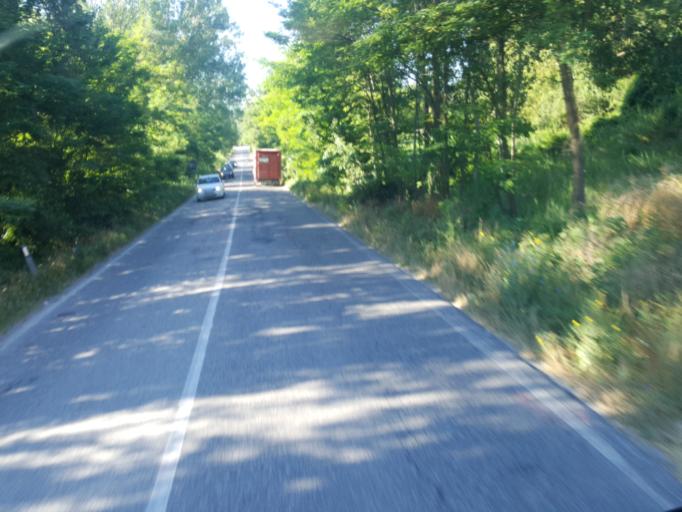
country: IT
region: The Marches
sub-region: Provincia di Pesaro e Urbino
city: Borgo Massano
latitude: 43.8097
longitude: 12.6610
